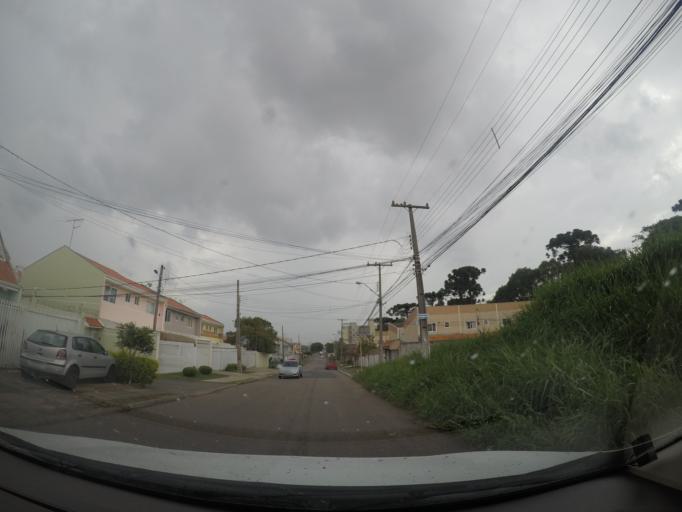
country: BR
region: Parana
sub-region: Sao Jose Dos Pinhais
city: Sao Jose dos Pinhais
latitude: -25.5203
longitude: -49.2591
